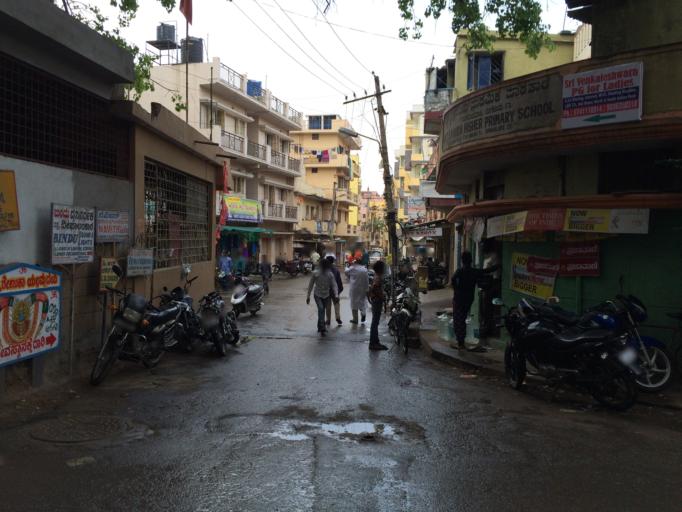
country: IN
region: Karnataka
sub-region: Bangalore Urban
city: Bangalore
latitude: 12.9897
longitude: 77.6638
